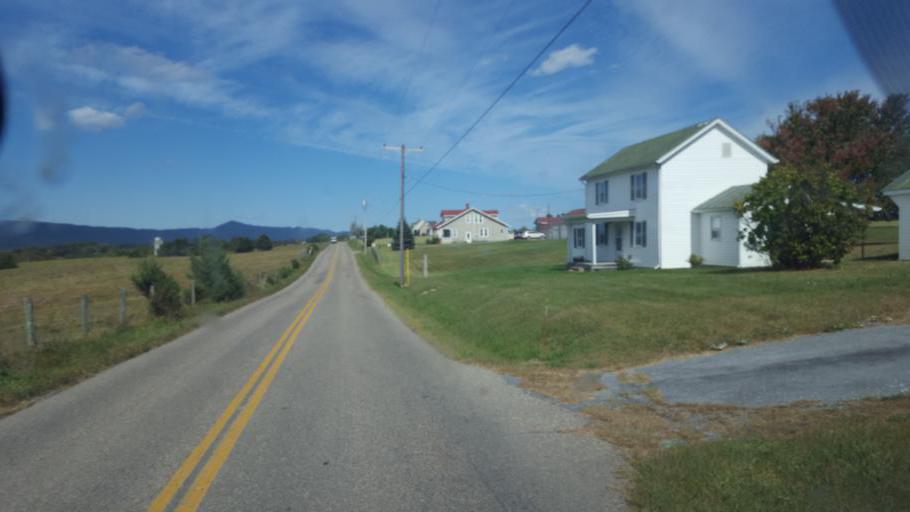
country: US
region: Virginia
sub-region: Page County
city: Stanley
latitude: 38.6207
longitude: -78.5291
